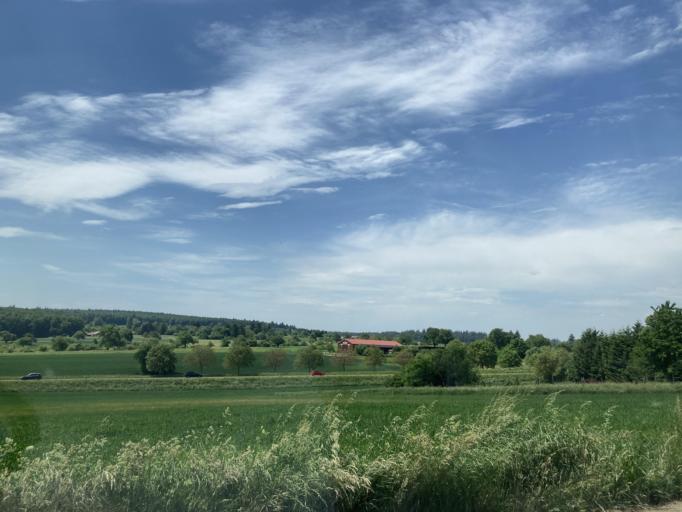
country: DE
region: Baden-Wuerttemberg
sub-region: Karlsruhe Region
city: Konigsbach-Stein
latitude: 48.9142
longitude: 8.5223
